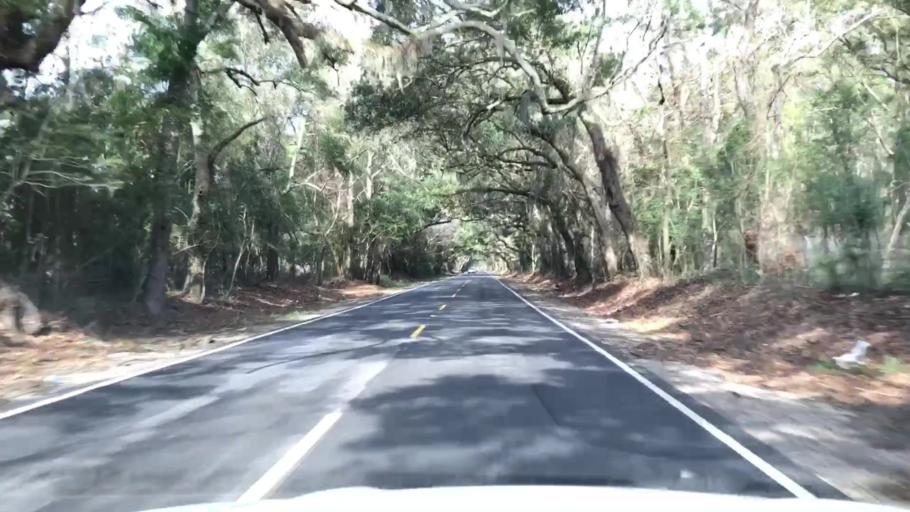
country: US
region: South Carolina
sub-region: Charleston County
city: Folly Beach
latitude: 32.7074
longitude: -80.0169
